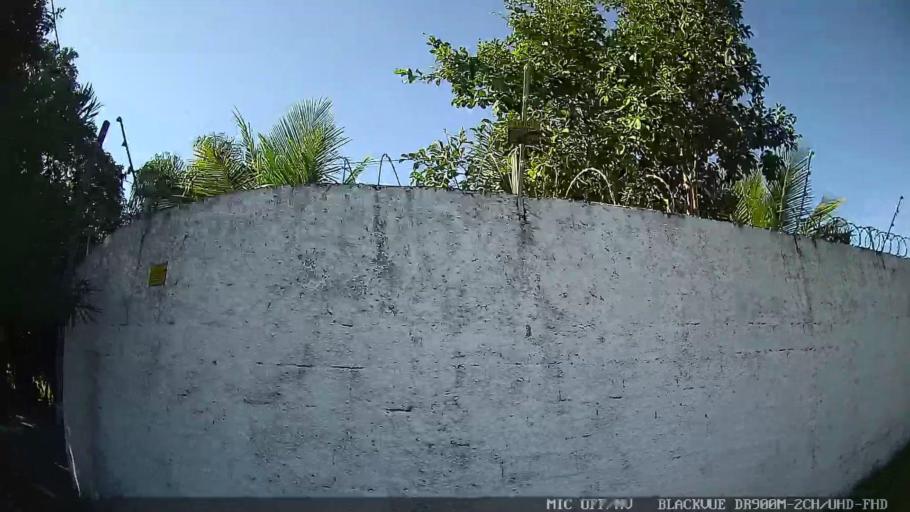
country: BR
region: Sao Paulo
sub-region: Peruibe
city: Peruibe
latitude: -24.2717
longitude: -46.9453
